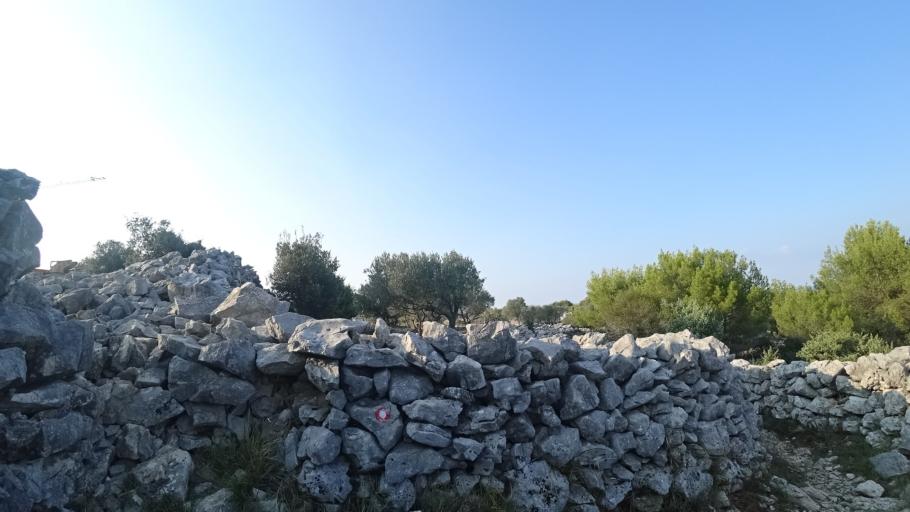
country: HR
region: Primorsko-Goranska
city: Mali Losinj
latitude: 44.5249
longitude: 14.4757
